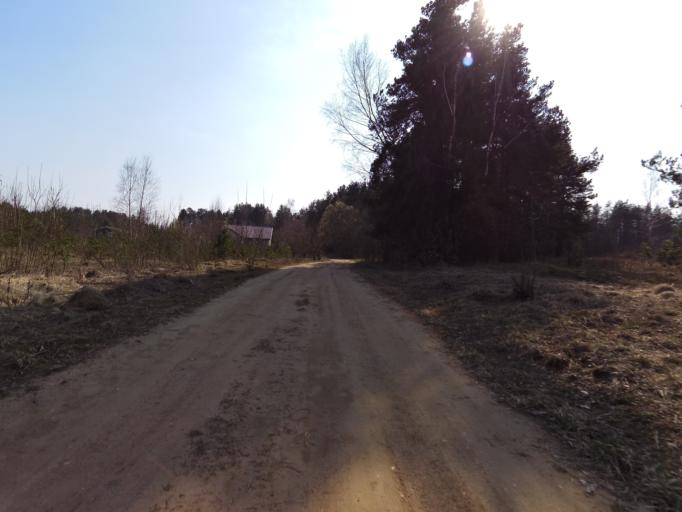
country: LT
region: Vilnius County
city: Pilaite
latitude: 54.6930
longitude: 25.1667
